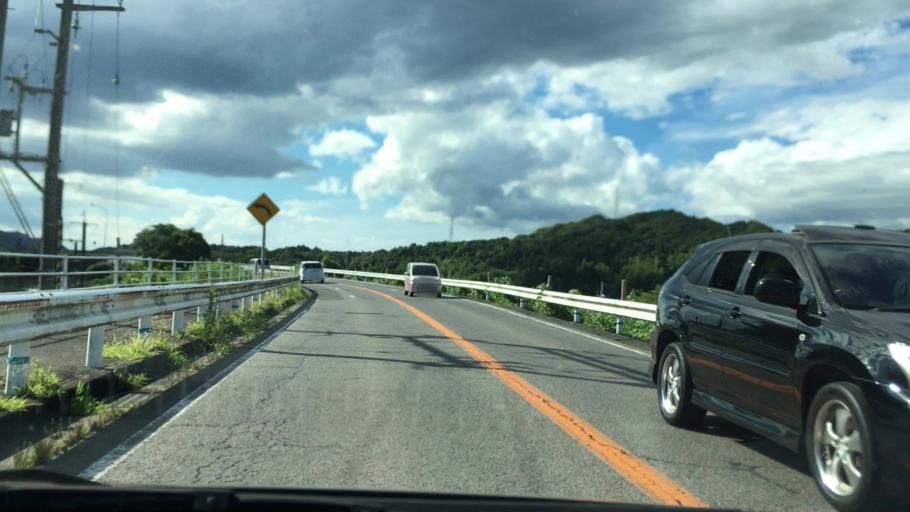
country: JP
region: Saga Prefecture
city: Takeocho-takeo
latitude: 33.1952
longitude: 129.9790
